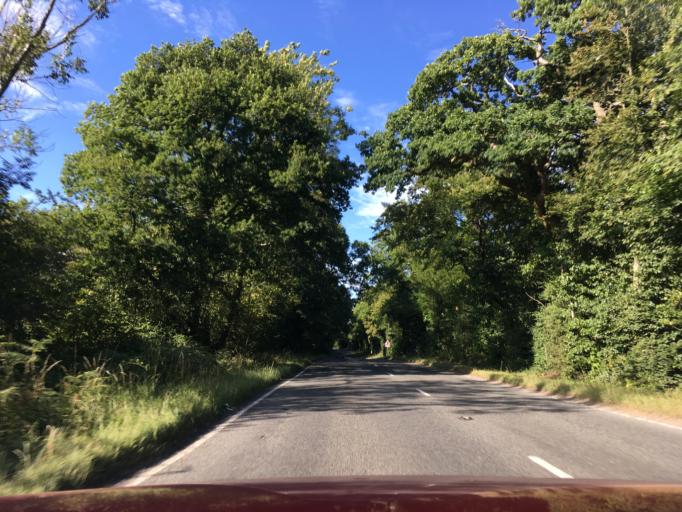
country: GB
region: England
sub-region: Hampshire
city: Romsey
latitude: 50.9608
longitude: -1.5275
